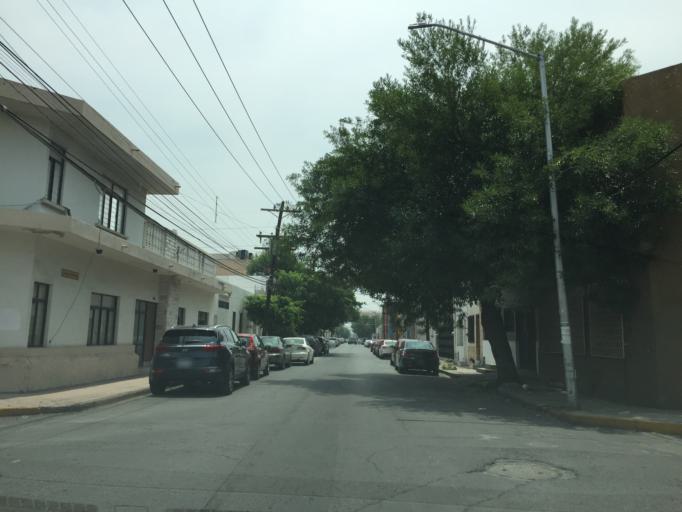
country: MX
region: Nuevo Leon
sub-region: Monterrey
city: Monterrey
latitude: 25.6799
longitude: -100.3004
